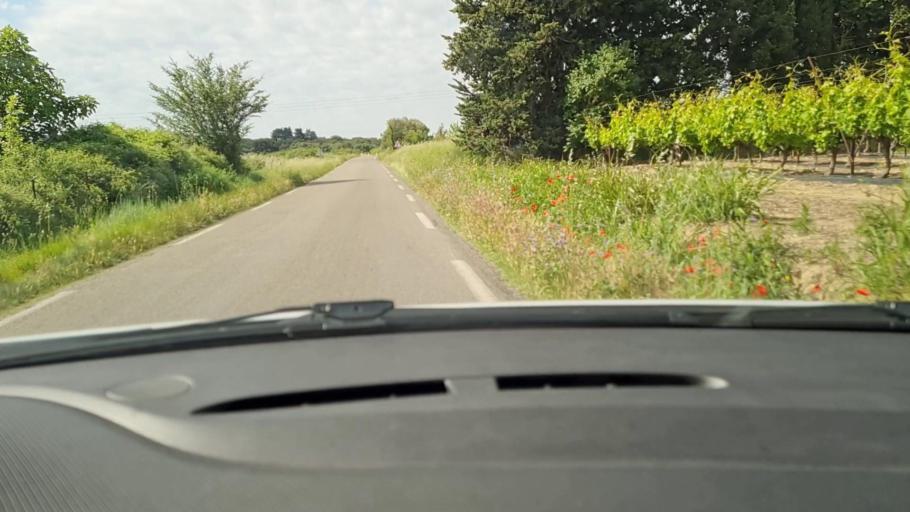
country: FR
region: Languedoc-Roussillon
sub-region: Departement du Gard
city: Jonquieres-Saint-Vincent
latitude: 43.8198
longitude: 4.5570
